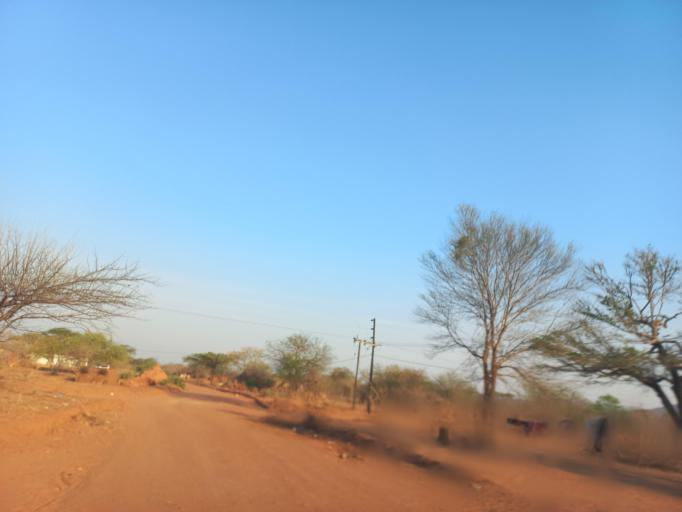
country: ZM
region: Lusaka
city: Luangwa
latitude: -15.4454
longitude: 30.3663
